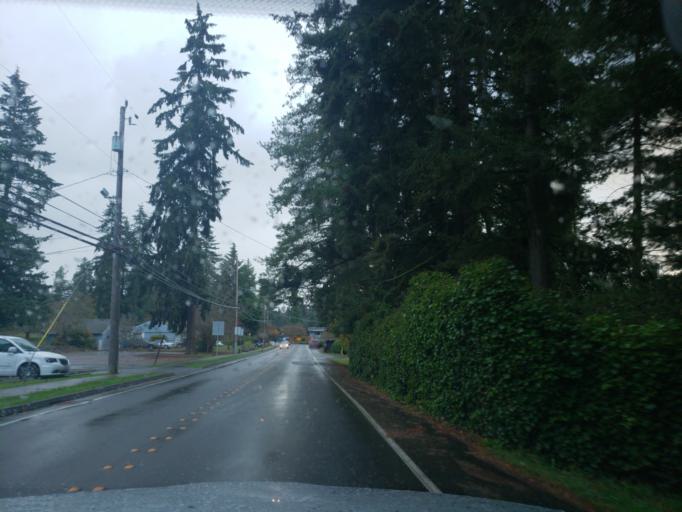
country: US
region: Washington
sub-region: King County
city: Shoreline
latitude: 47.7502
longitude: -122.3509
